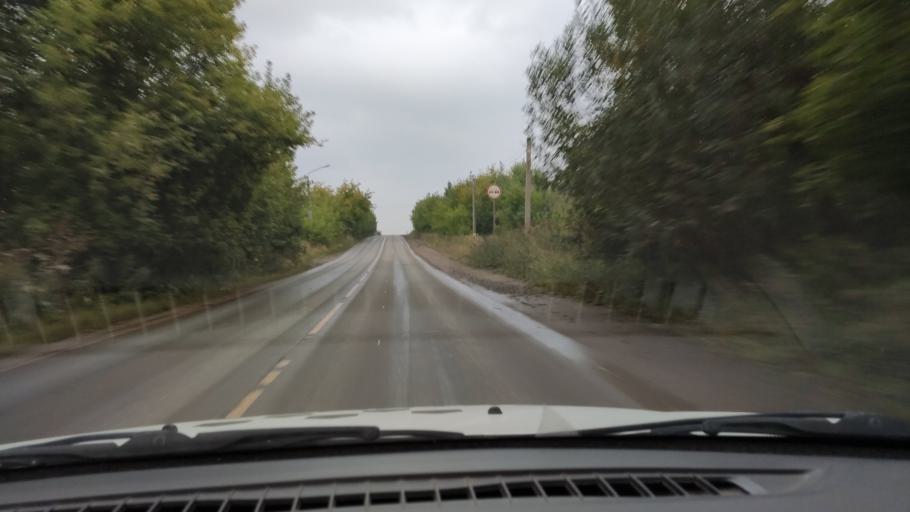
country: RU
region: Perm
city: Gamovo
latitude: 57.9082
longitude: 56.1649
